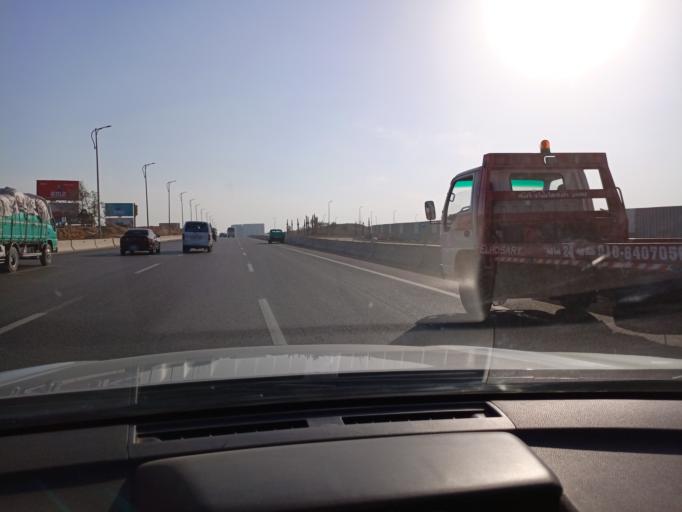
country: EG
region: Muhafazat al Qalyubiyah
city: Al Khankah
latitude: 30.0606
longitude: 31.4157
